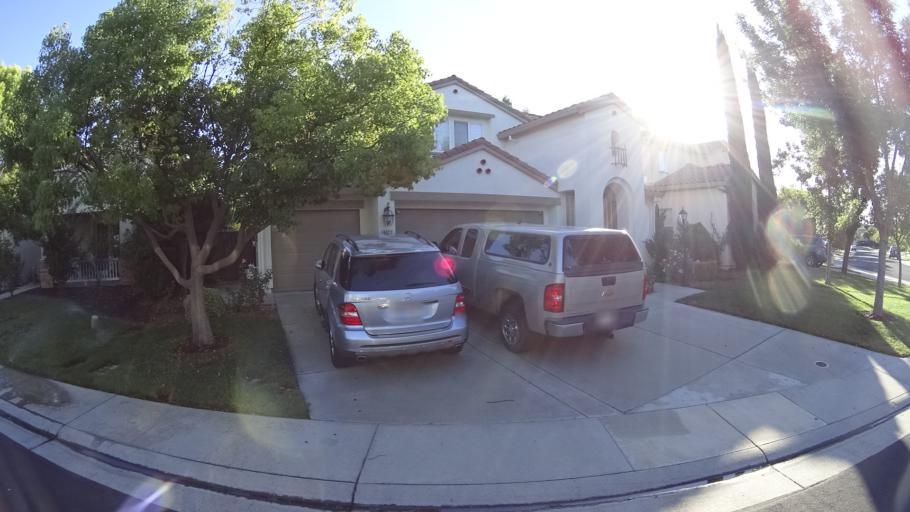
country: US
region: California
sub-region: Sacramento County
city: Laguna
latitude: 38.4006
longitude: -121.4766
